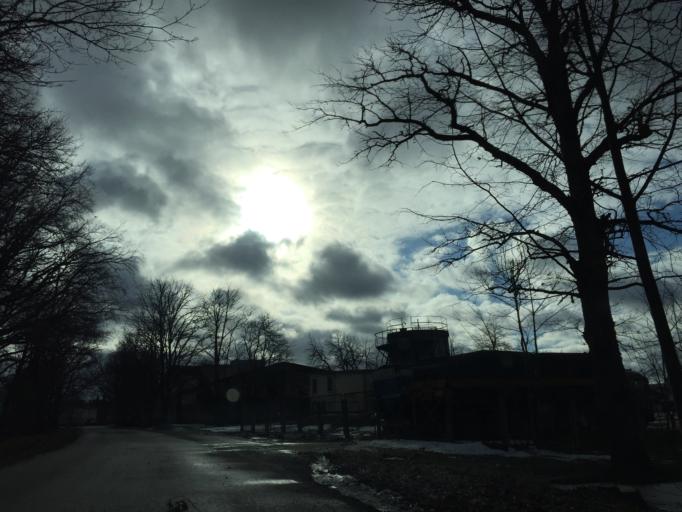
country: LV
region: Aloja
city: Aloja
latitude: 57.7732
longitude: 24.8131
